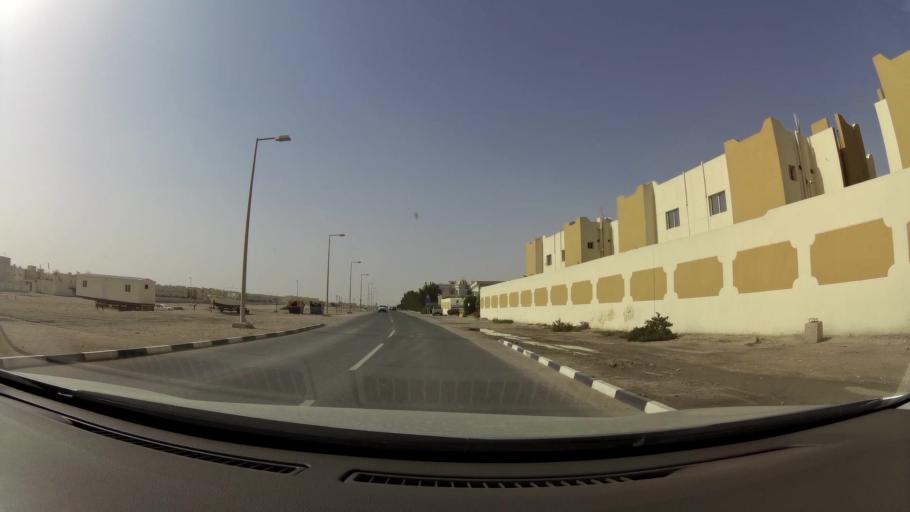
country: QA
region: Baladiyat ar Rayyan
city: Ar Rayyan
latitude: 25.3434
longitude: 51.4545
